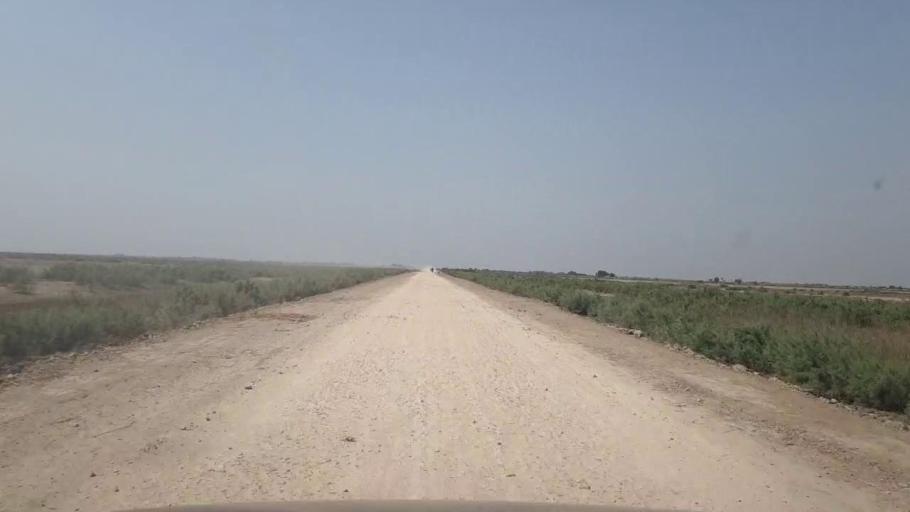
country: PK
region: Sindh
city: Jati
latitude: 24.3761
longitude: 68.5742
